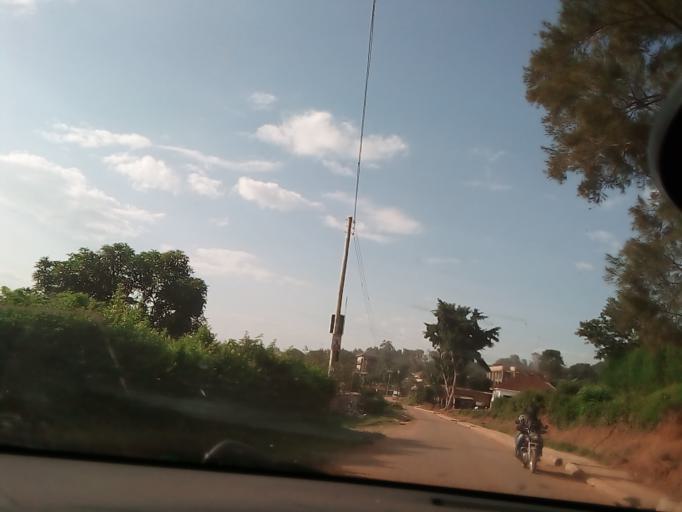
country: UG
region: Central Region
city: Masaka
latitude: -0.3533
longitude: 31.7437
